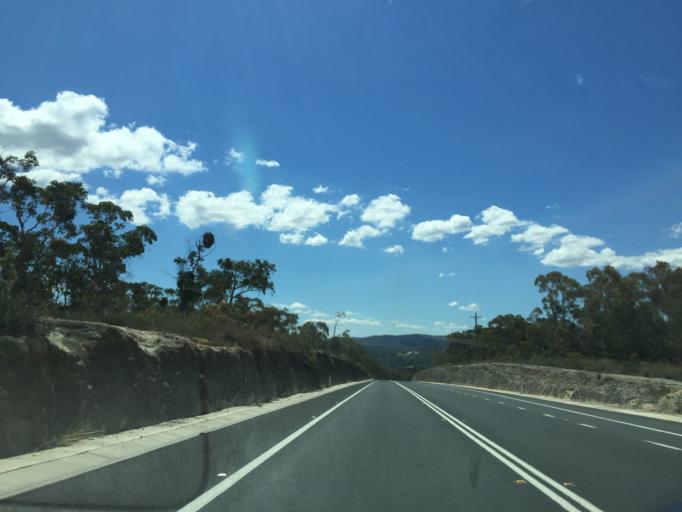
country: AU
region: New South Wales
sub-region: Lithgow
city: Lithgow
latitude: -33.4177
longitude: 150.1011
